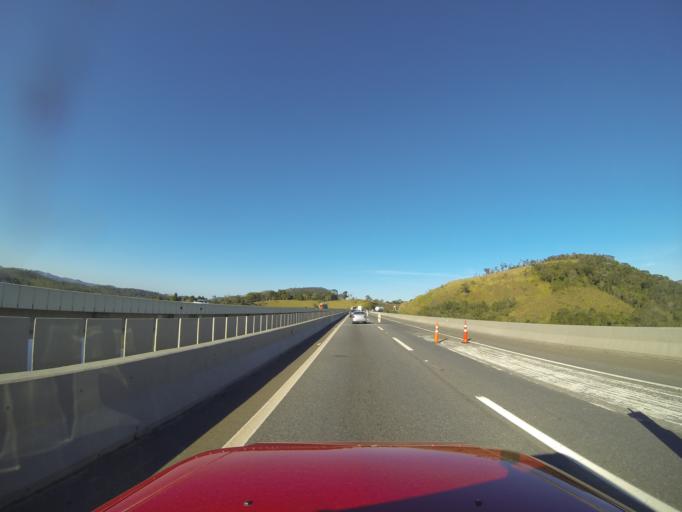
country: BR
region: Sao Paulo
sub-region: Bom Jesus Dos Perdoes
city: Bom Jesus dos Perdoes
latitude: -23.1854
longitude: -46.3659
